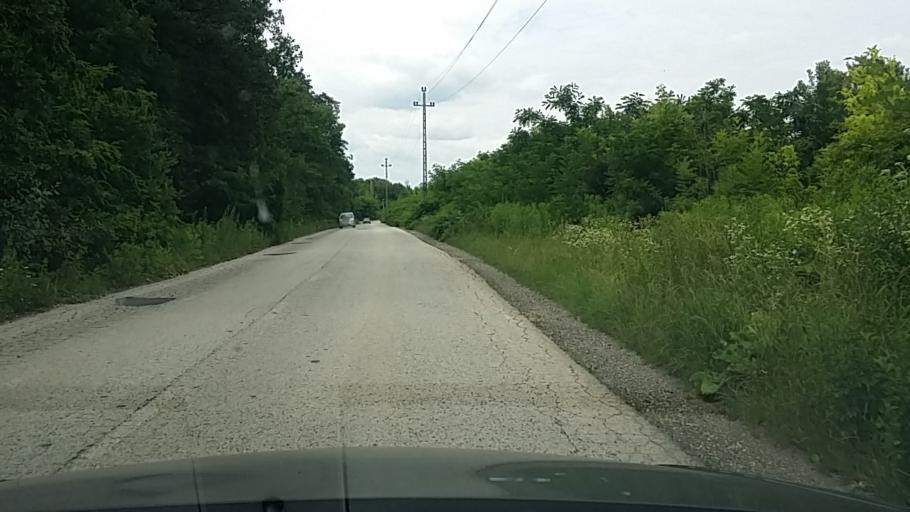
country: HU
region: Pest
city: Godollo
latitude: 47.6085
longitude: 19.3298
